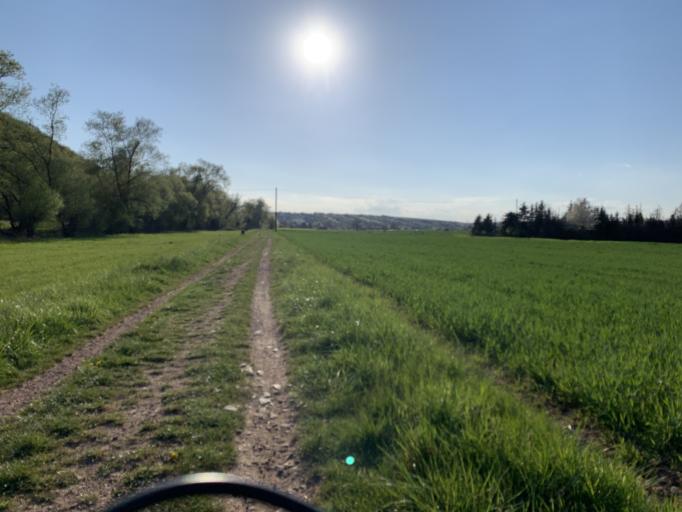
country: DE
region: Rheinland-Pfalz
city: Dorsheim
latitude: 49.8886
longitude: 7.8703
